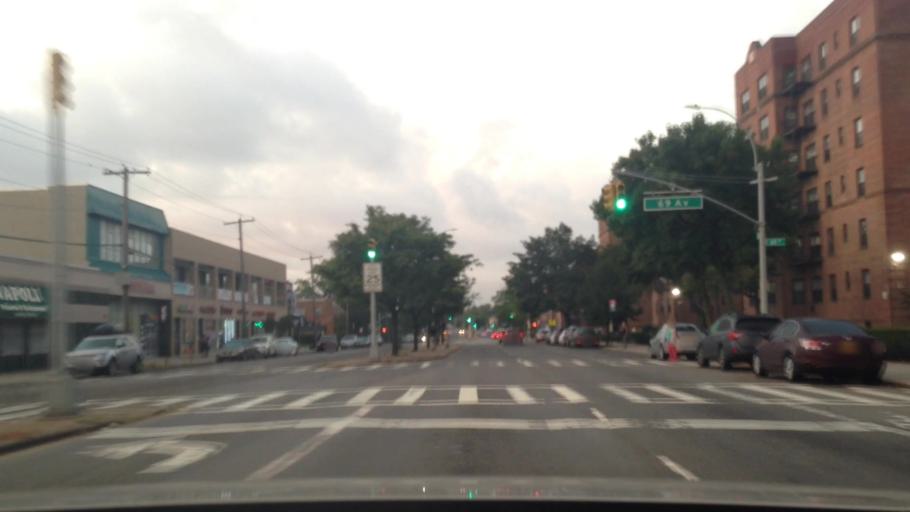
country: US
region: New York
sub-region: Queens County
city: Jamaica
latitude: 40.7333
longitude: -73.8050
